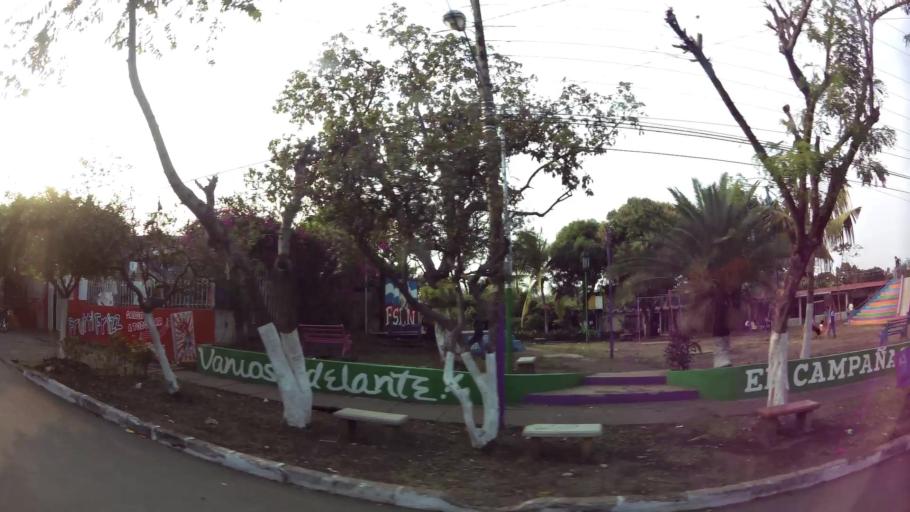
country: NI
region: Masaya
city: Masaya
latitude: 11.9807
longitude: -86.0773
